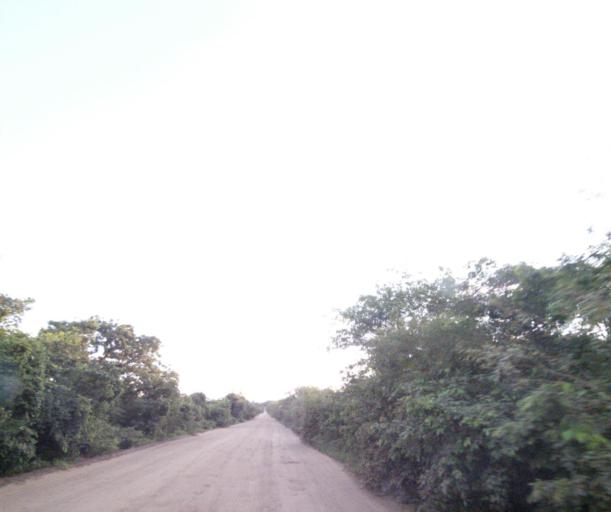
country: BR
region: Bahia
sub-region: Sao Felix Do Coribe
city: Santa Maria da Vitoria
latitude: -13.6410
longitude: -44.4389
